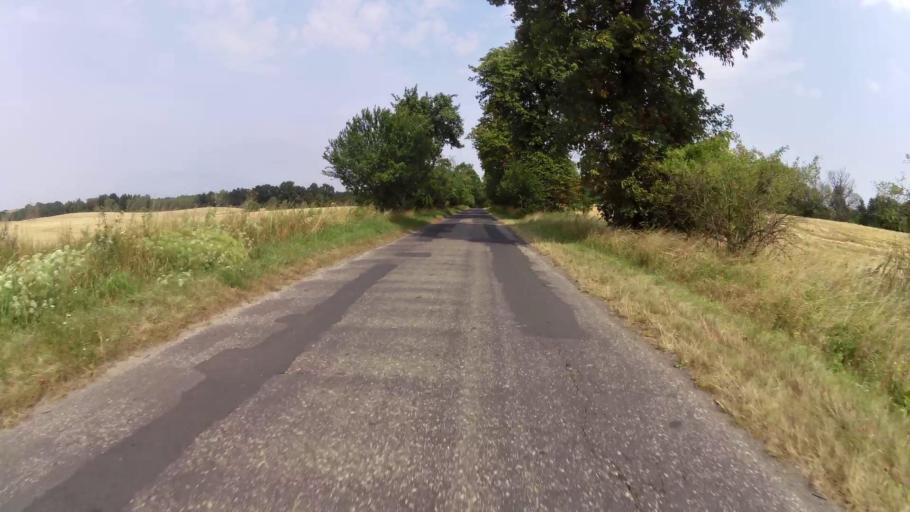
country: PL
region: West Pomeranian Voivodeship
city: Trzcinsko Zdroj
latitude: 52.8976
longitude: 14.5298
